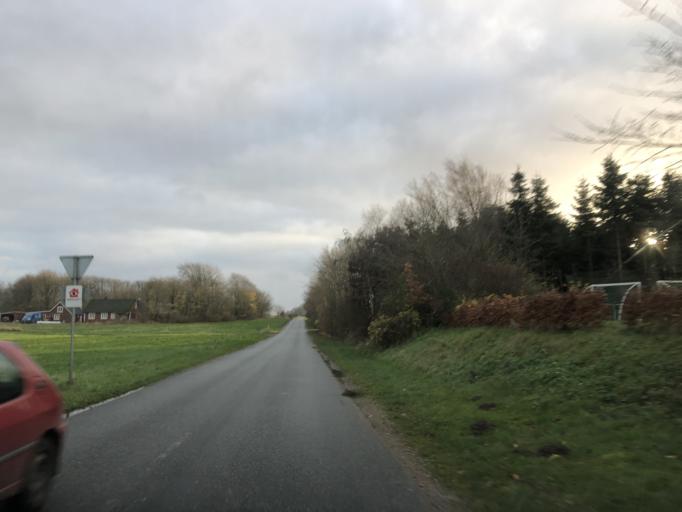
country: DK
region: Central Jutland
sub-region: Viborg Kommune
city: Viborg
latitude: 56.5000
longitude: 9.3453
